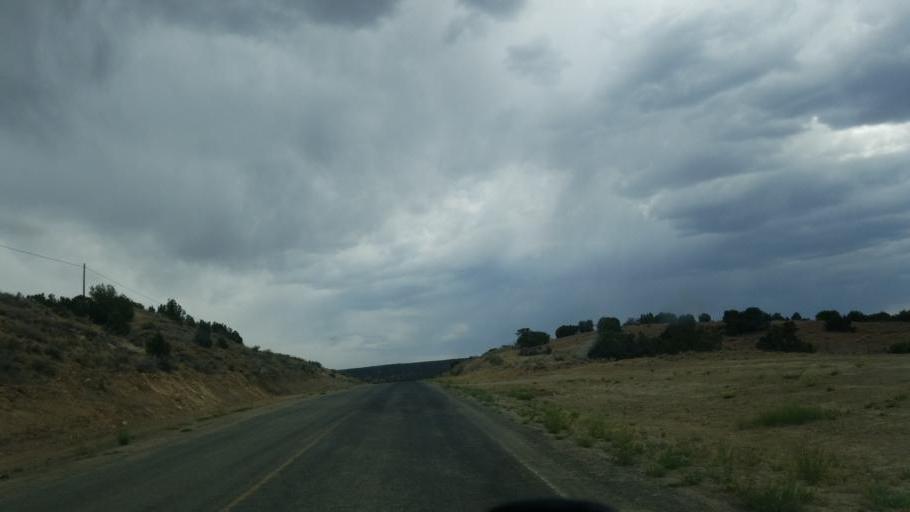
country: US
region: Arizona
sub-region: Apache County
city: Saint Michaels
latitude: 35.4230
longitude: -108.9791
